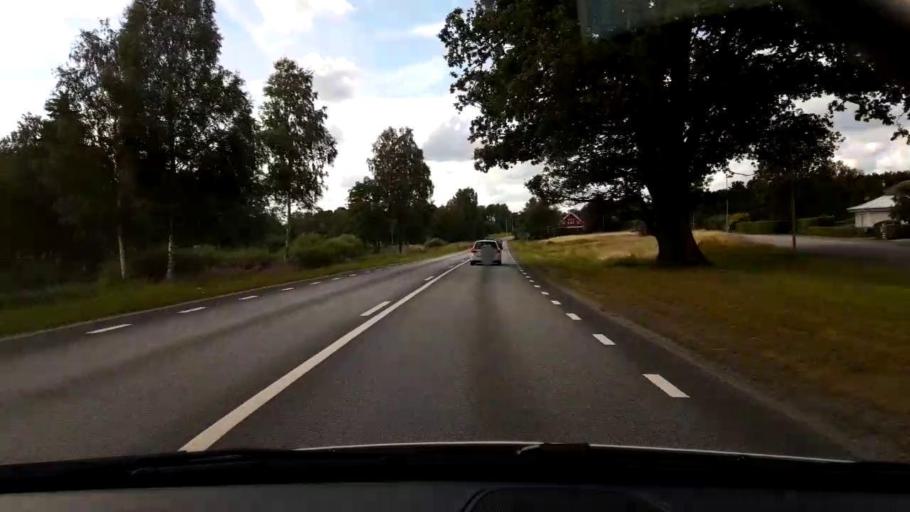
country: SE
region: Joenkoeping
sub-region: Savsjo Kommun
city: Vrigstad
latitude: 57.3583
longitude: 14.4611
